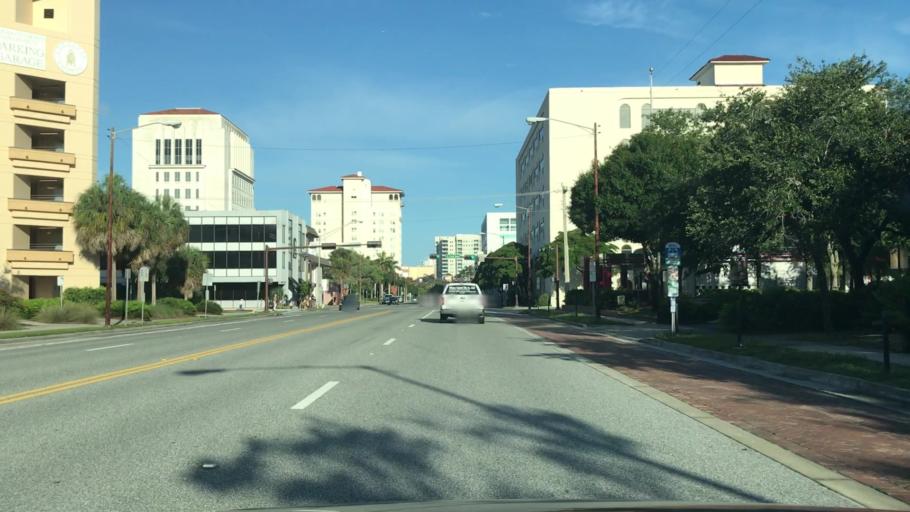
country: US
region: Florida
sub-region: Sarasota County
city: Sarasota
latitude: 27.3357
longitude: -82.5274
